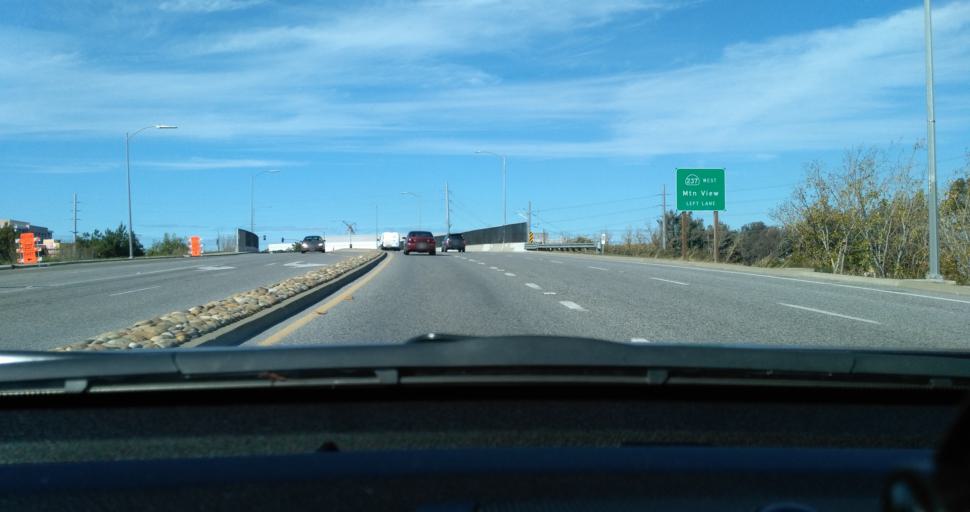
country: US
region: California
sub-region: Santa Clara County
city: Milpitas
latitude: 37.4182
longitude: -121.9584
